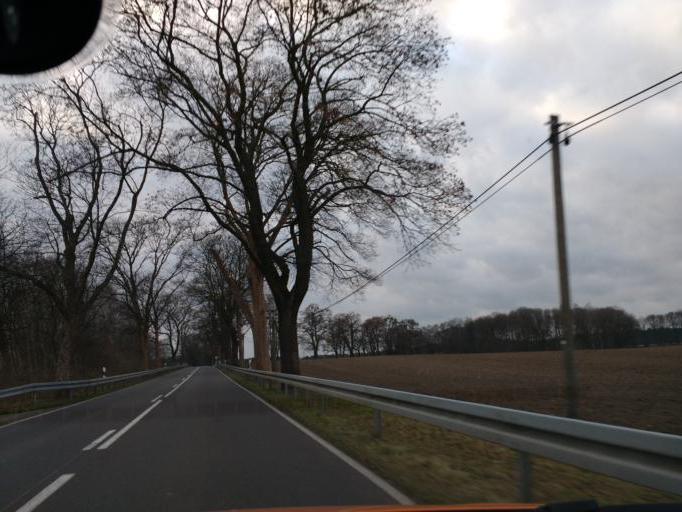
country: DE
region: Brandenburg
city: Protzel
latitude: 52.6560
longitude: 14.0317
